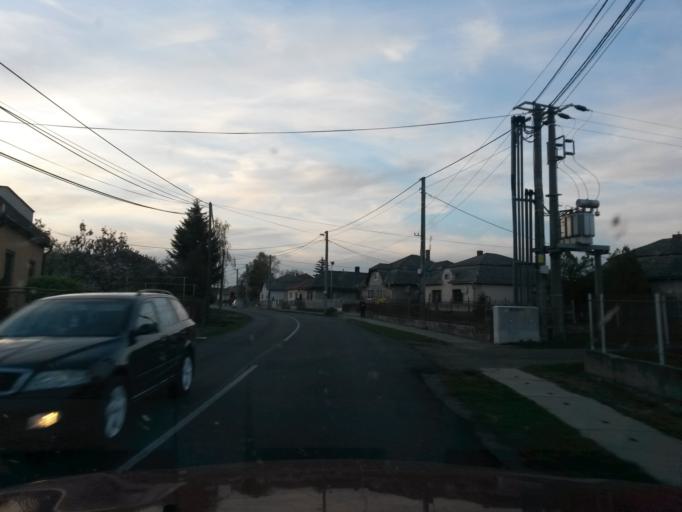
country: HU
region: Borsod-Abauj-Zemplen
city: Satoraljaujhely
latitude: 48.5290
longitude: 21.5820
